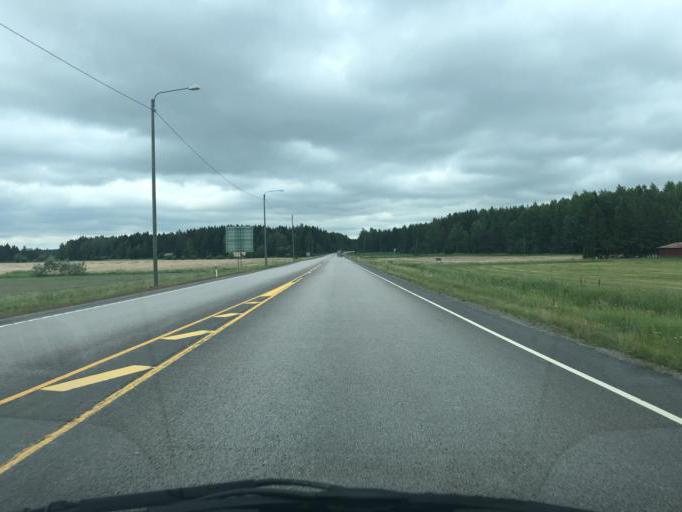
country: FI
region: Uusimaa
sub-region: Loviisa
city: Lapinjaervi
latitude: 60.6731
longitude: 26.2527
